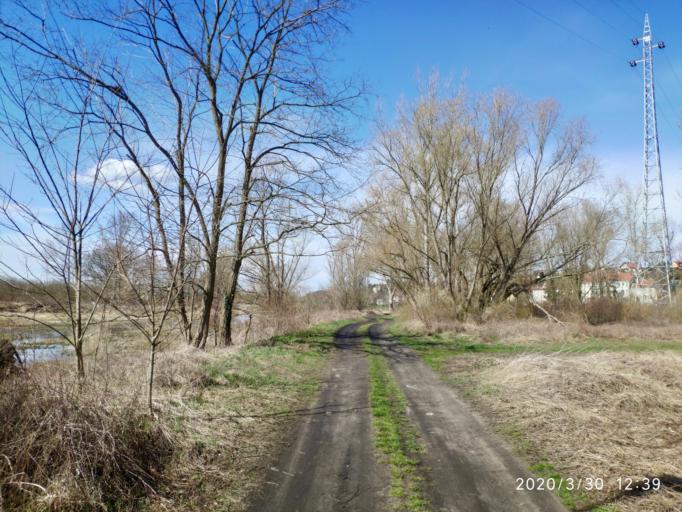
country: PL
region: Lubusz
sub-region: Powiat krosnienski
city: Krosno Odrzanskie
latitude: 52.0487
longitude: 15.0931
